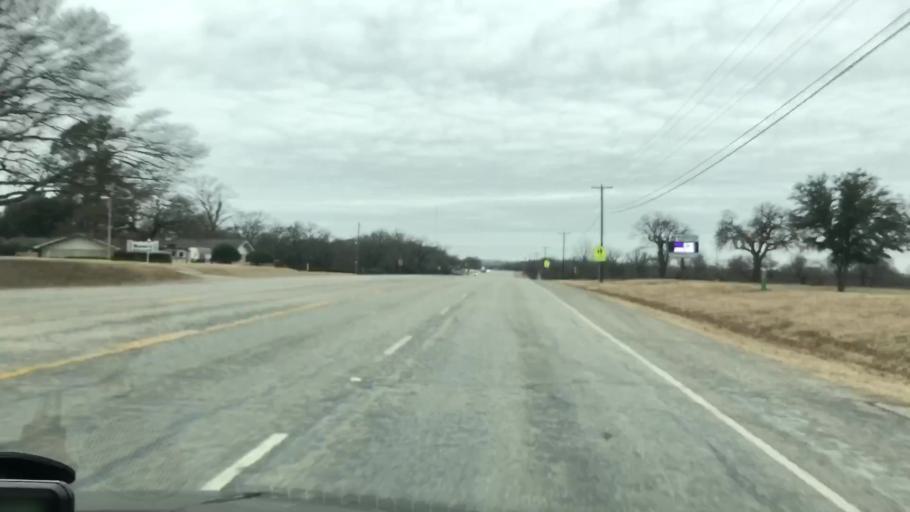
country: US
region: Texas
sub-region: Jack County
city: Jacksboro
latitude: 33.2276
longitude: -98.1690
